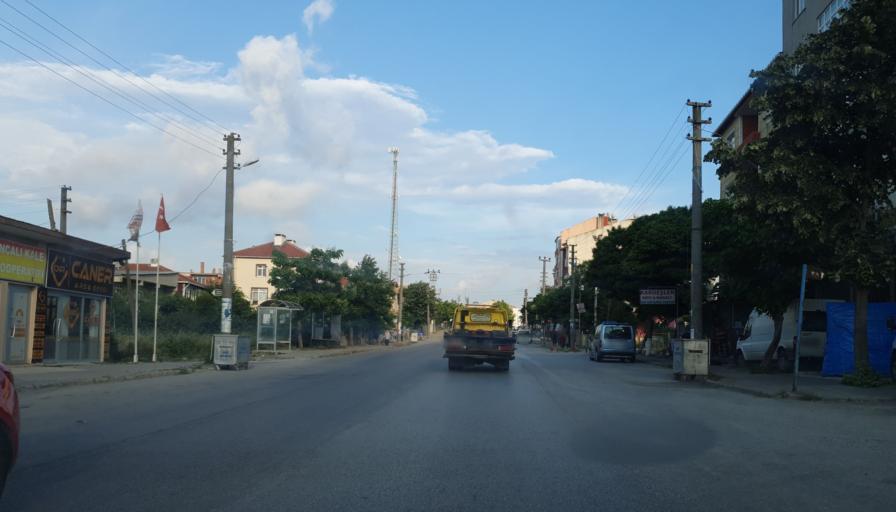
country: TR
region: Tekirdag
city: Cerkezkoey
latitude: 41.3585
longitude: 27.9491
